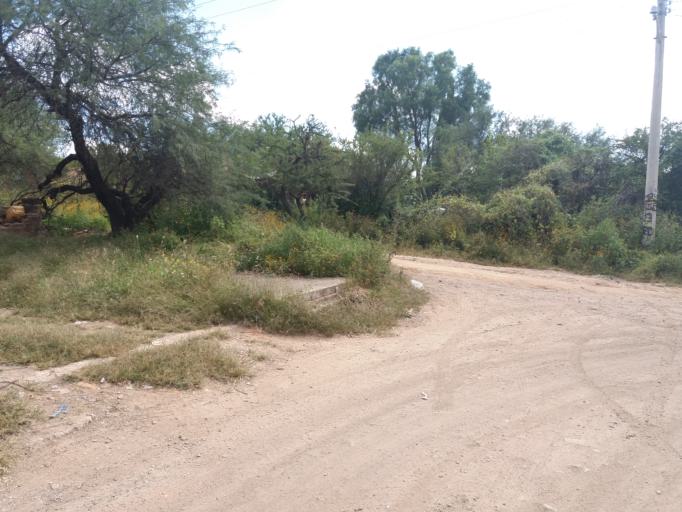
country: MX
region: Aguascalientes
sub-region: Aguascalientes
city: San Sebastian [Fraccionamiento]
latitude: 21.8057
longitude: -102.2427
